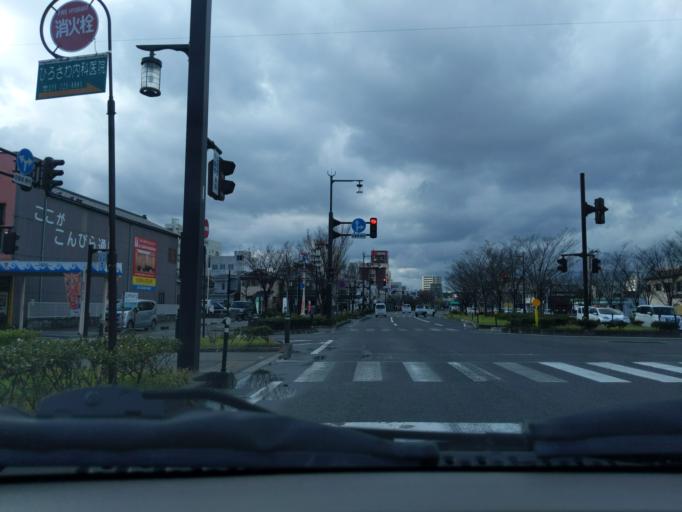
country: JP
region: Niigata
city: Niigata-shi
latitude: 37.9255
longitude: 139.0507
